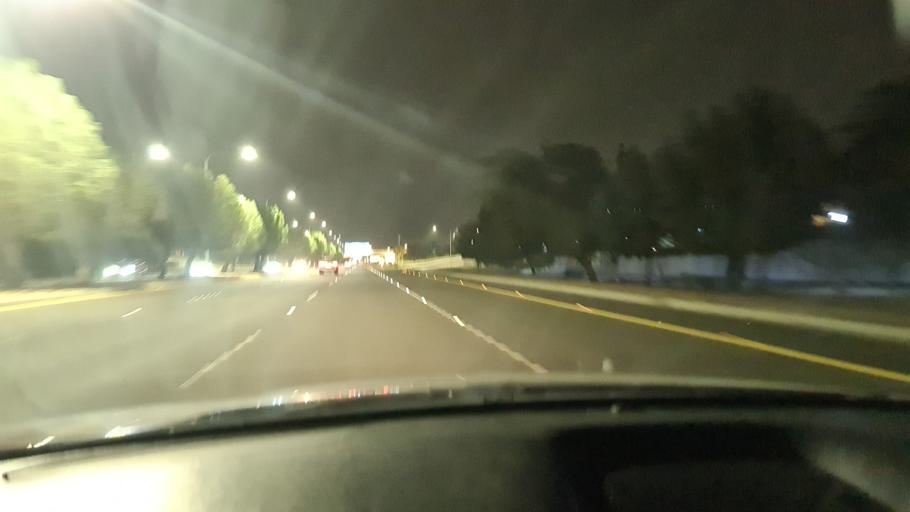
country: SA
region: Eastern Province
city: Al Jubayl
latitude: 27.1271
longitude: 49.5465
